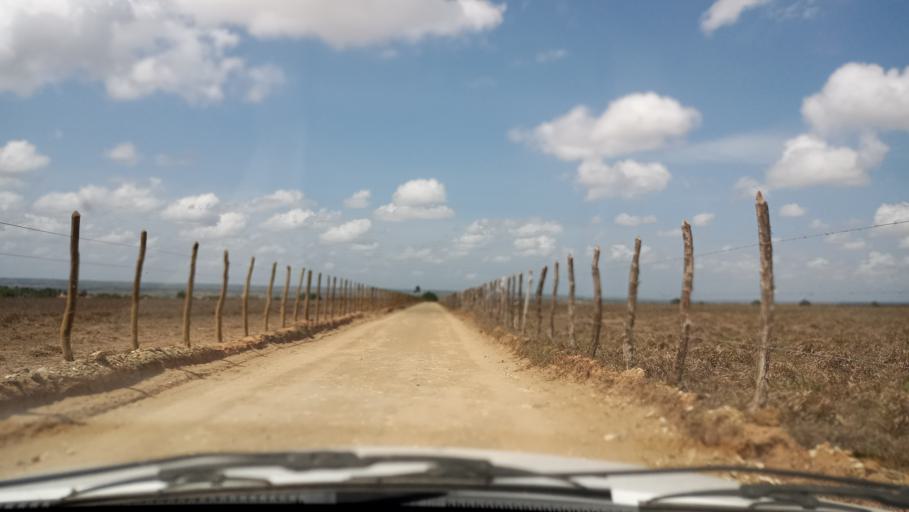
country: BR
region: Rio Grande do Norte
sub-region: Pedro Velho
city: Pedro Velho
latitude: -6.3506
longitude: -35.3326
